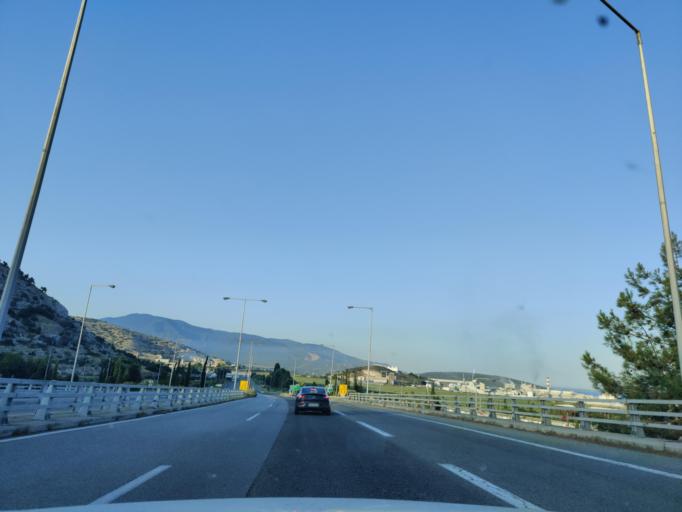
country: GR
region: East Macedonia and Thrace
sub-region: Nomos Kavalas
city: Nea Karvali
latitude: 40.9547
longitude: 24.4626
